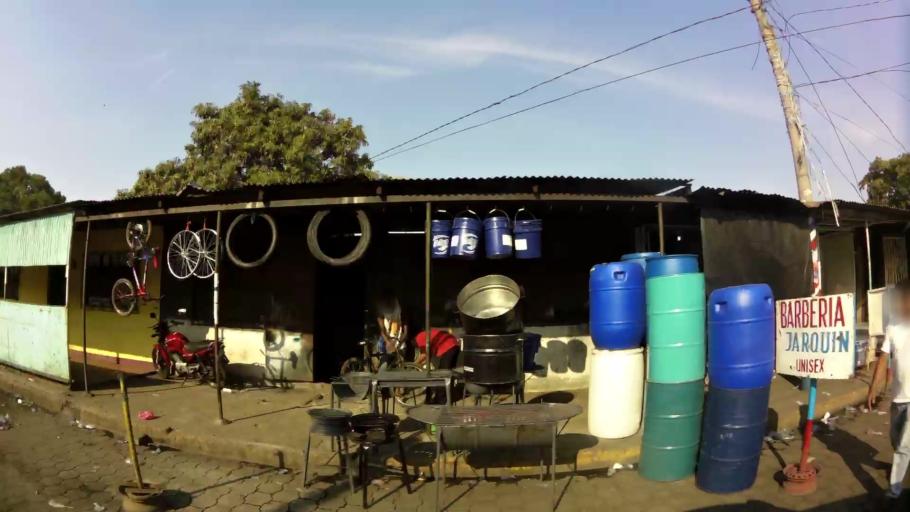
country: NI
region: Managua
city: Managua
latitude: 12.1447
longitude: -86.2603
